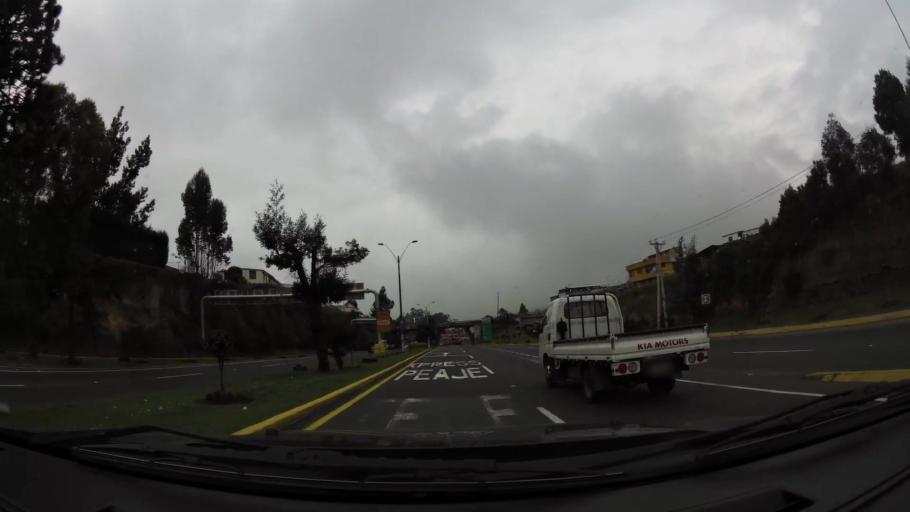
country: EC
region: Pichincha
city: Quito
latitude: -0.2390
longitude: -78.4850
